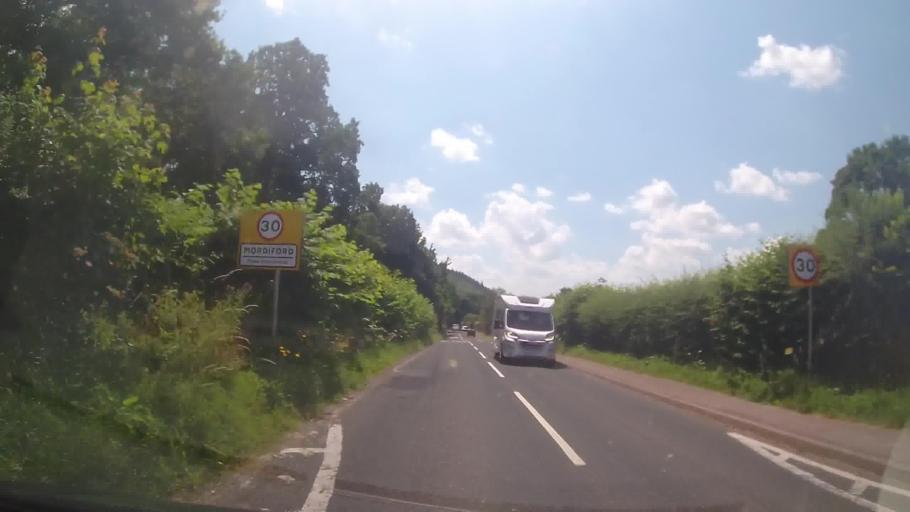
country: GB
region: England
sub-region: Herefordshire
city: Withington
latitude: 52.0353
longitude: -2.6260
